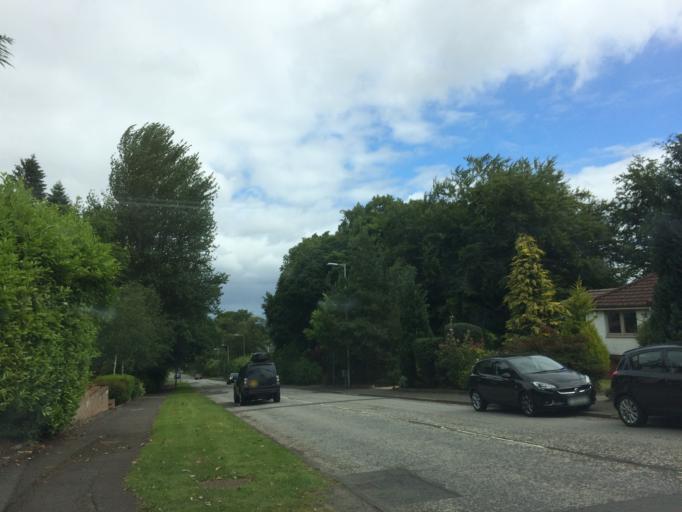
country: GB
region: Scotland
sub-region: East Renfrewshire
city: Newton Mearns
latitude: 55.7750
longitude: -4.3331
